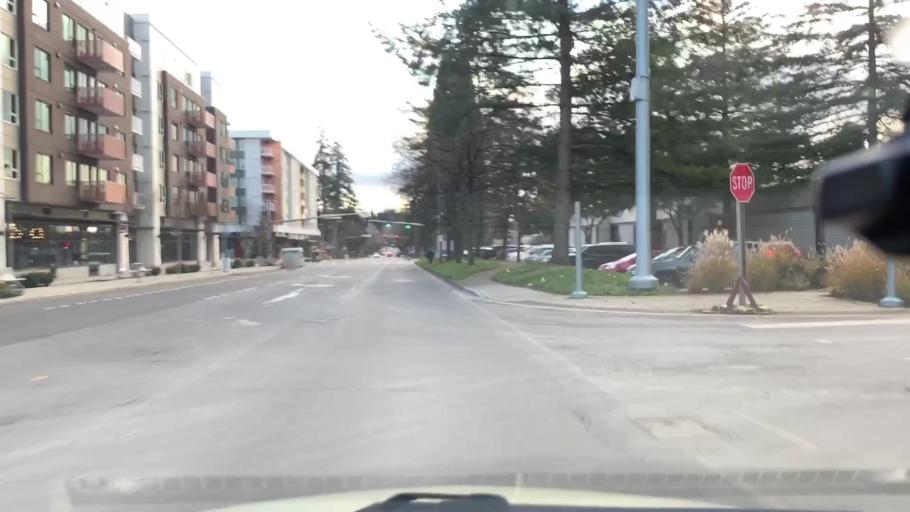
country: US
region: Washington
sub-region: King County
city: Redmond
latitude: 47.6352
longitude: -122.1377
